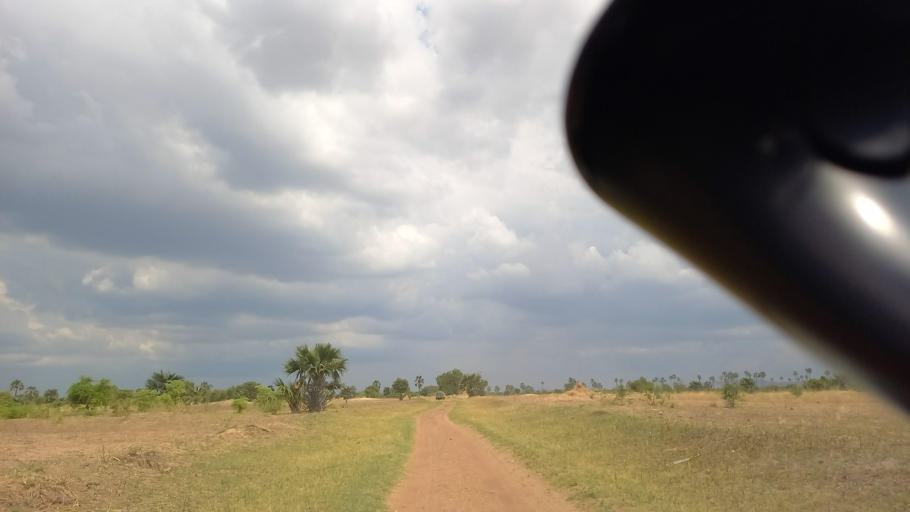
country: ZM
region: Lusaka
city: Kafue
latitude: -15.8302
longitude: 28.0621
